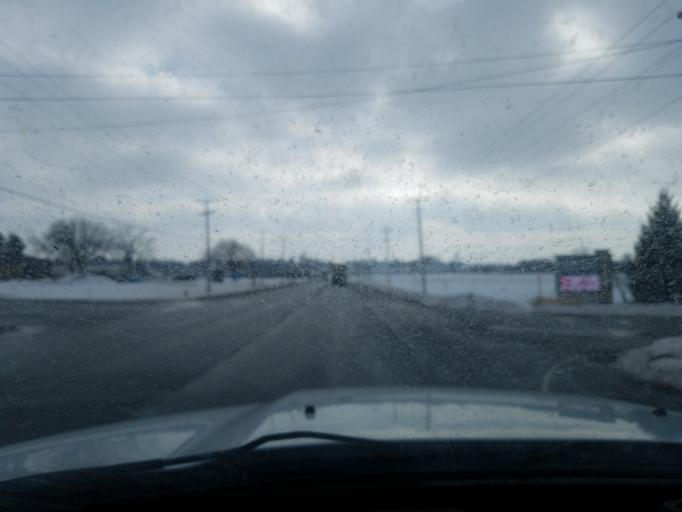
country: US
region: Indiana
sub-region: Marshall County
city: Bremen
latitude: 41.4567
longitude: -86.1563
